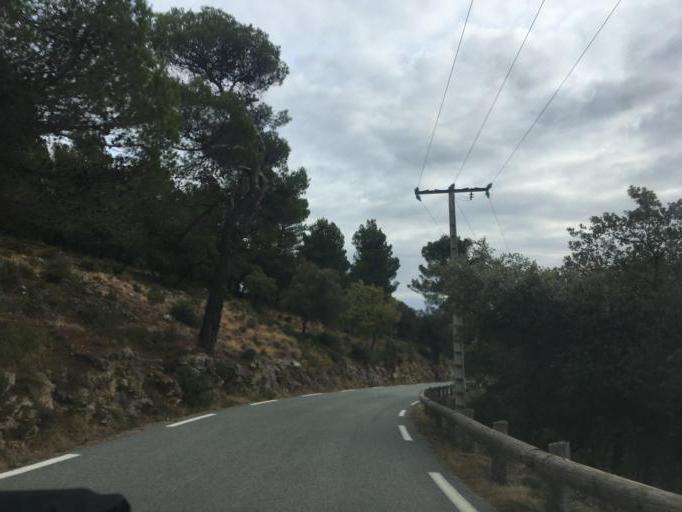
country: FR
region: Provence-Alpes-Cote d'Azur
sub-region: Departement du Var
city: Villecroze
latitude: 43.5759
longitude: 6.3173
